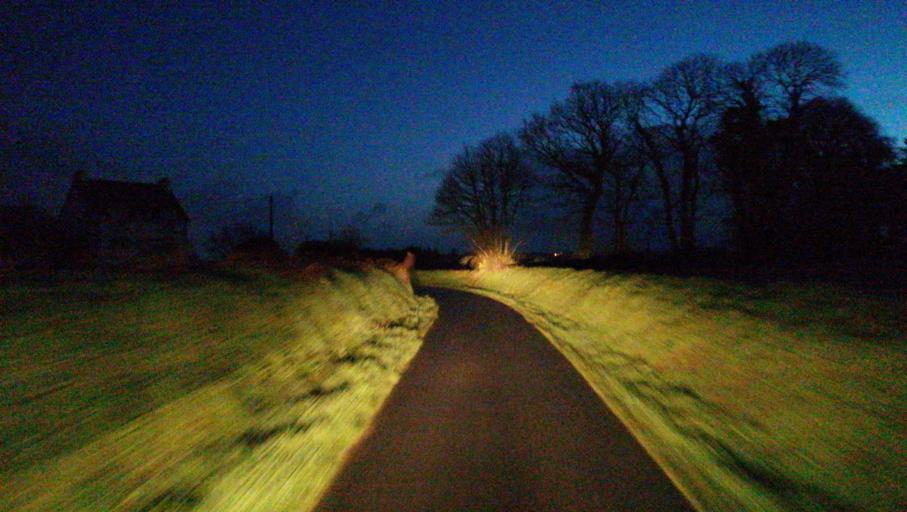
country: FR
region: Brittany
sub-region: Departement des Cotes-d'Armor
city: Pommerit-le-Vicomte
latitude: 48.6581
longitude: -3.0564
